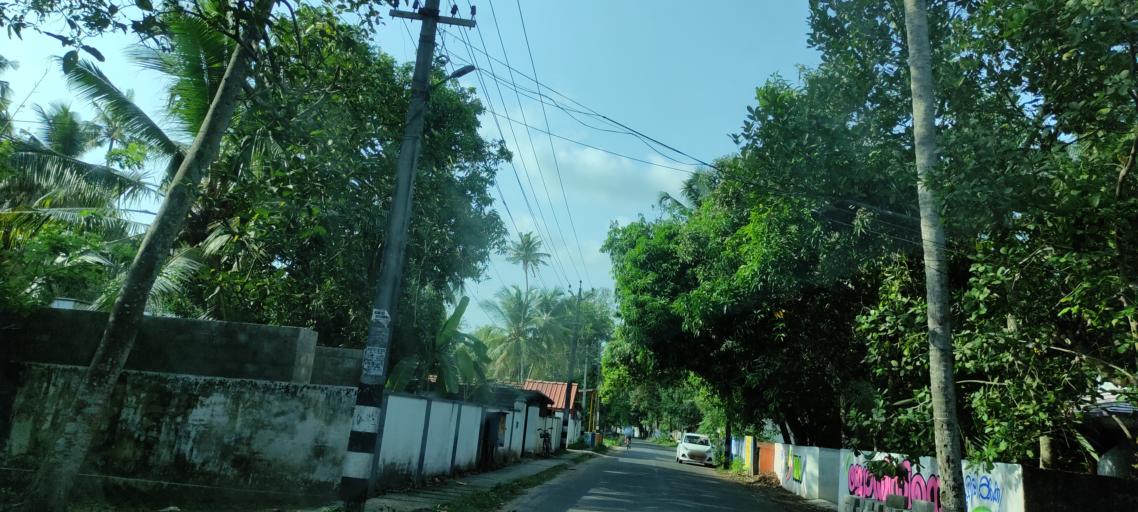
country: IN
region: Kerala
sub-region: Alappuzha
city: Vayalar
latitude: 9.6912
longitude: 76.2907
